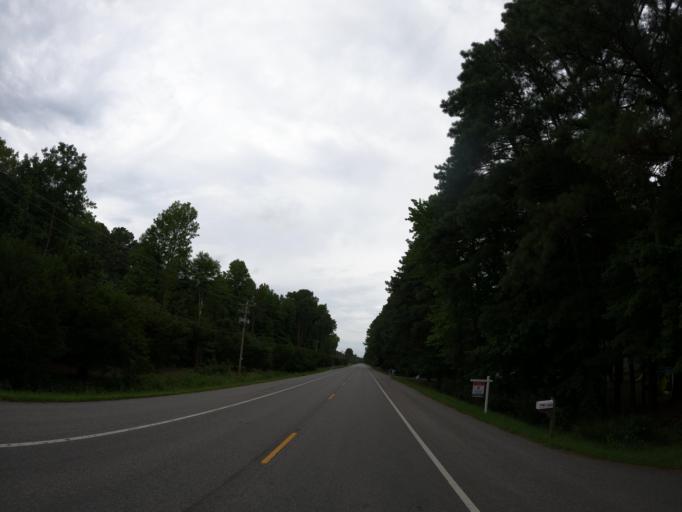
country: US
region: Maryland
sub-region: Saint Mary's County
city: Lexington Park
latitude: 38.1572
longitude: -76.5217
